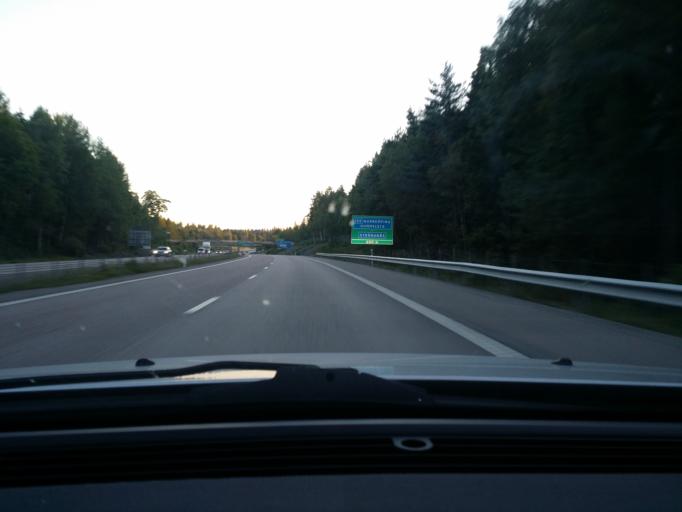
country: SE
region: Uppsala
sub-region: Enkopings Kommun
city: Enkoping
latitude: 59.6517
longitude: 17.0659
